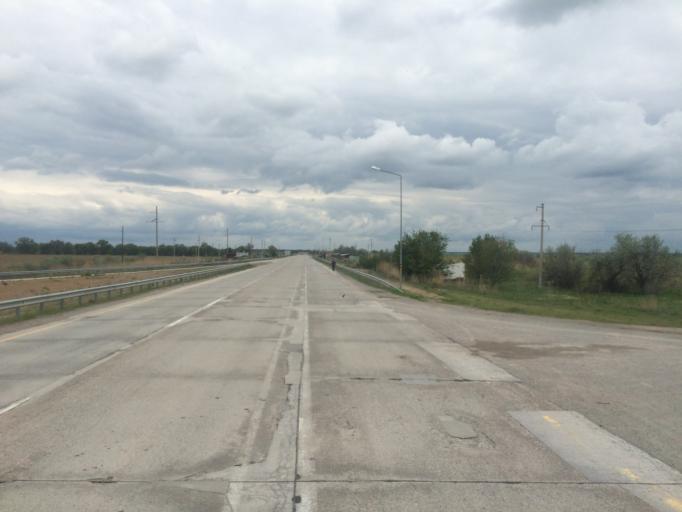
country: KG
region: Chuy
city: Sokuluk
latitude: 43.2729
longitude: 74.2359
